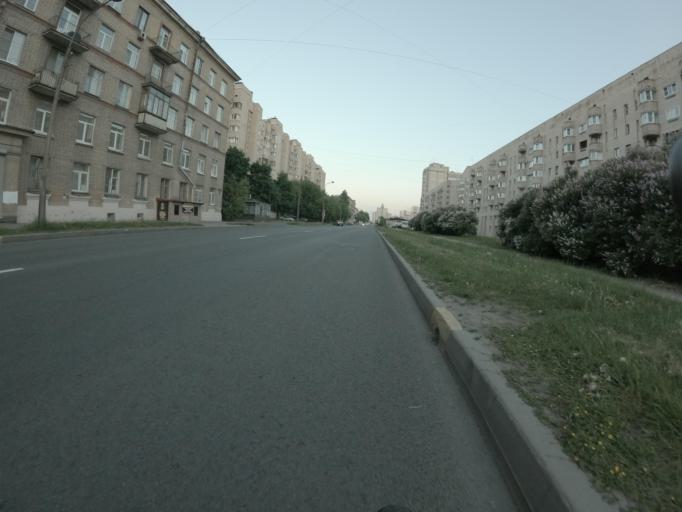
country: RU
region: St.-Petersburg
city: Kupchino
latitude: 59.8503
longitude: 30.3148
